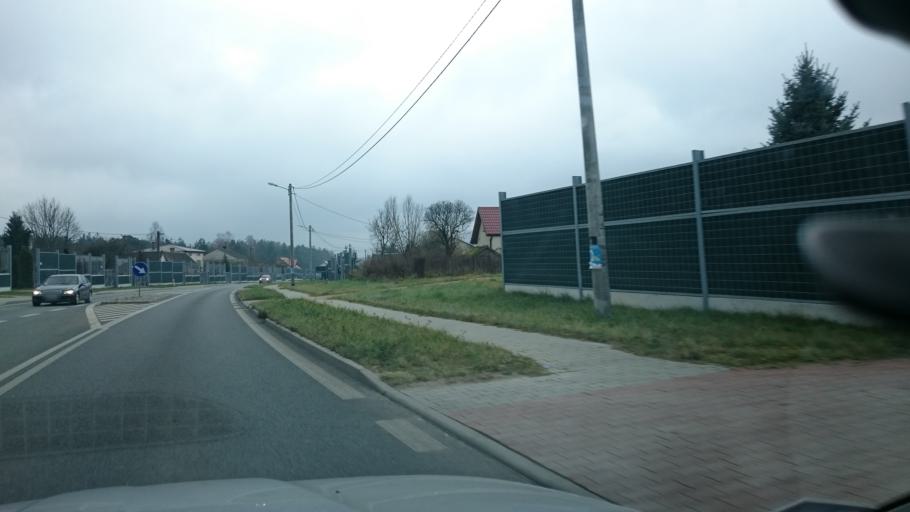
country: PL
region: Swietokrzyskie
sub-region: Powiat konecki
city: Konskie
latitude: 51.1416
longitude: 20.3644
